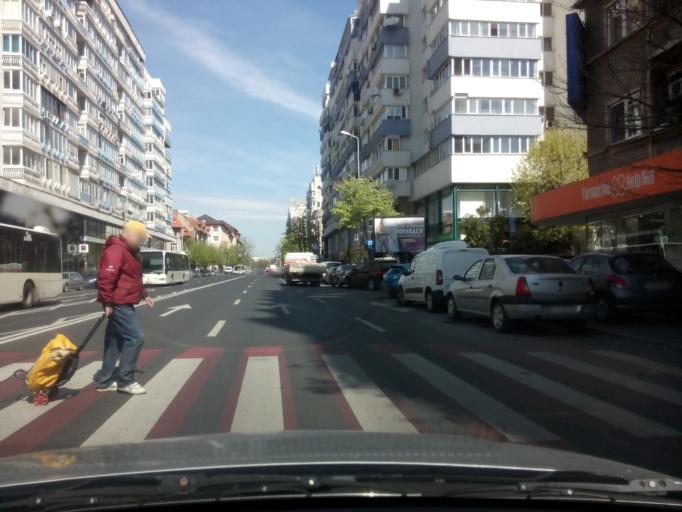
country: RO
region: Bucuresti
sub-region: Municipiul Bucuresti
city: Bucharest
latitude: 44.4559
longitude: 26.0972
